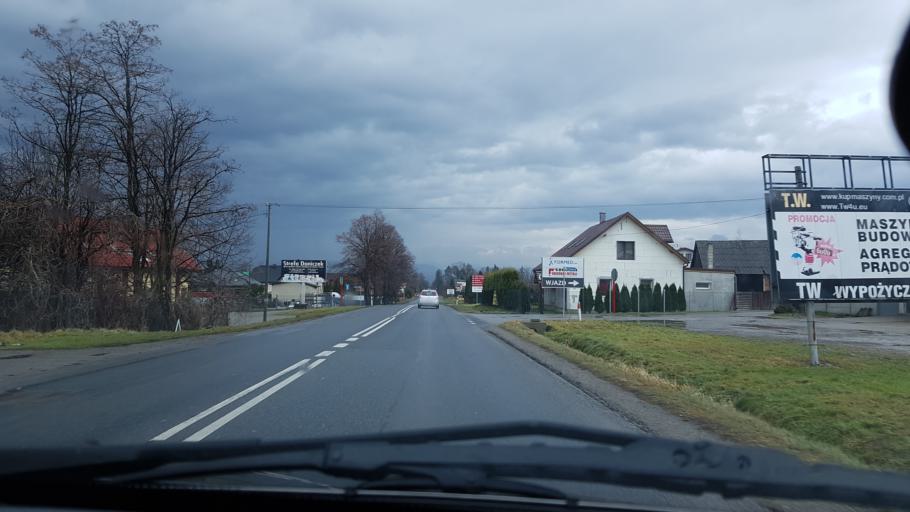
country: PL
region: Silesian Voivodeship
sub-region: Powiat zywiecki
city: Lodygowice
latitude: 49.7188
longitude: 19.1503
